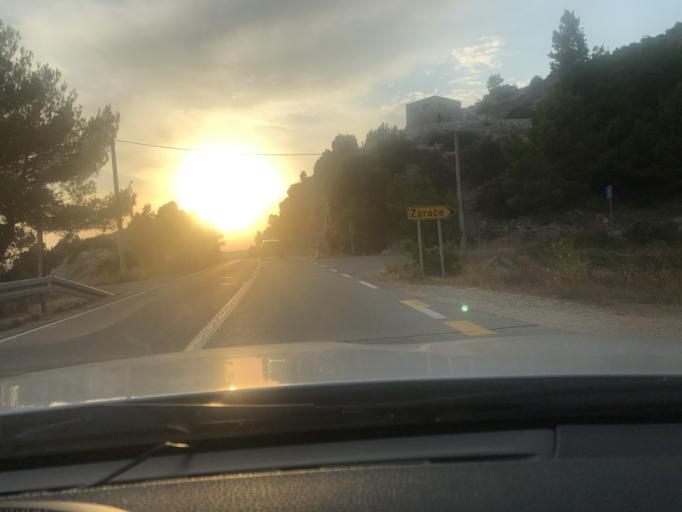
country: HR
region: Splitsko-Dalmatinska
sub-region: Grad Hvar
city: Hvar
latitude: 43.1525
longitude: 16.5147
